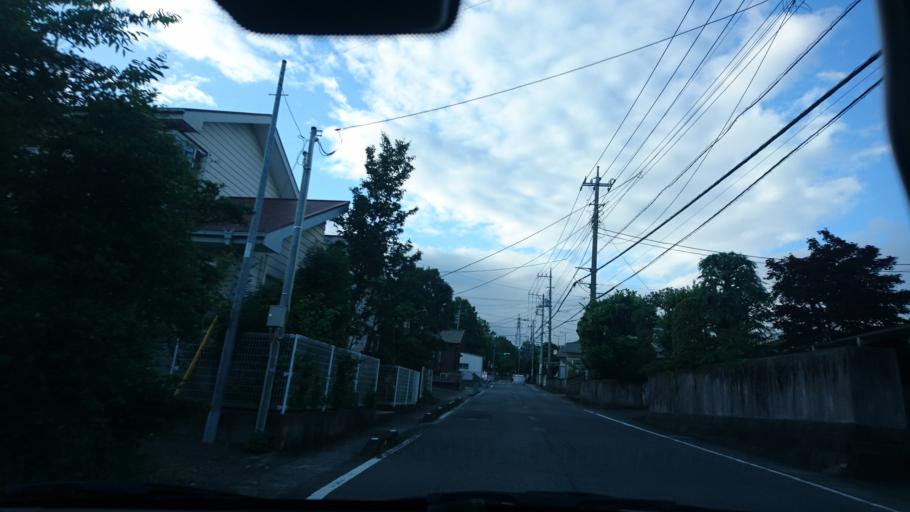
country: JP
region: Shizuoka
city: Fujinomiya
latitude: 35.2361
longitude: 138.6230
